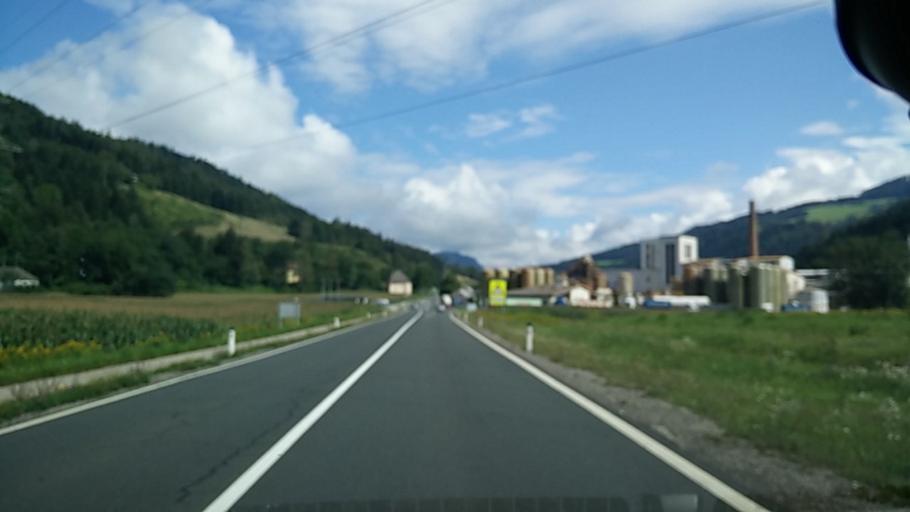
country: AT
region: Carinthia
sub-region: Politischer Bezirk Sankt Veit an der Glan
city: Bruckl
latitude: 46.7310
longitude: 14.5268
